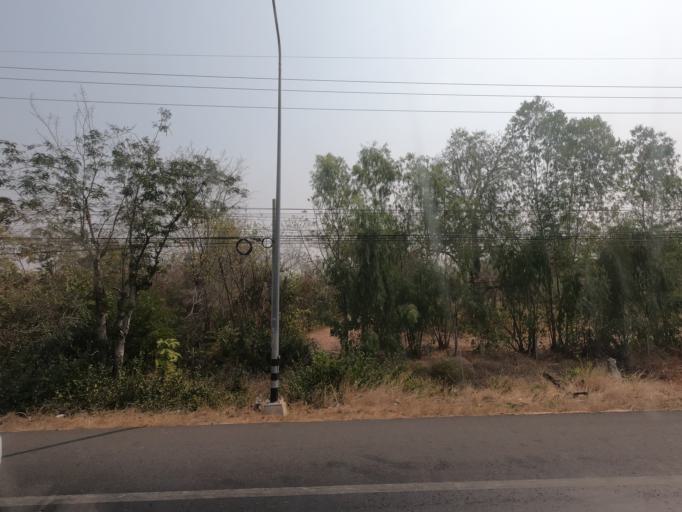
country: TH
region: Khon Kaen
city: Phon
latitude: 15.7627
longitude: 102.6065
